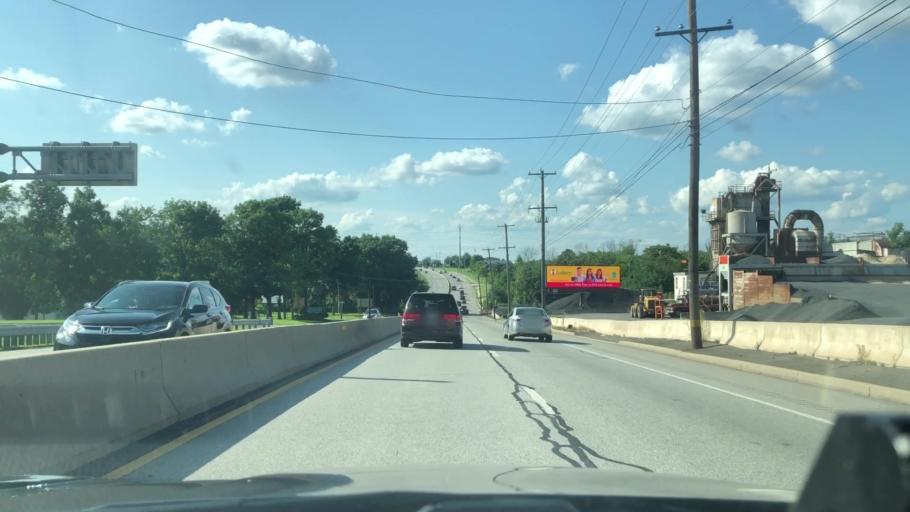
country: US
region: Pennsylvania
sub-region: Montgomery County
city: Montgomeryville
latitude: 40.2195
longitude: -75.2303
